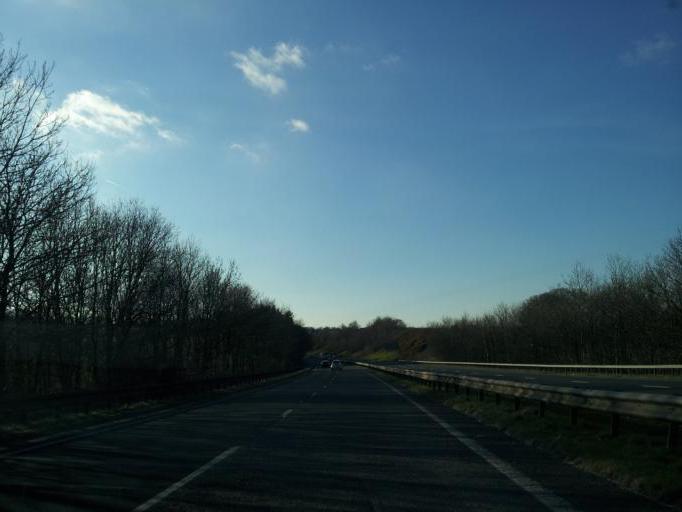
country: GB
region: England
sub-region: Devon
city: Crediton
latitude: 50.7290
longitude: -3.7330
